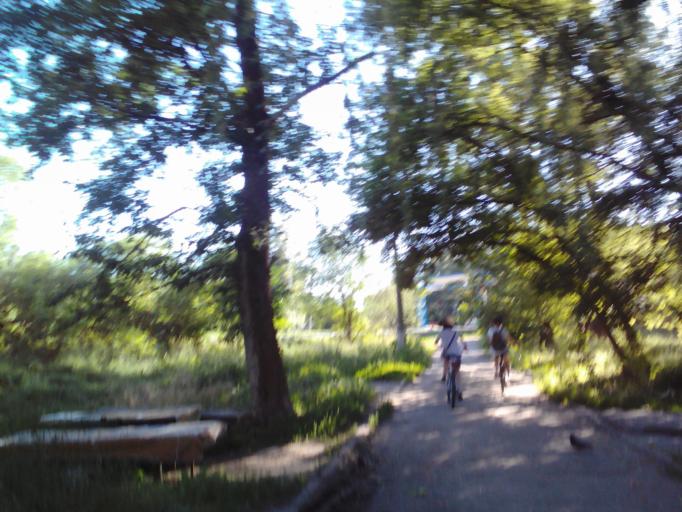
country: RU
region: Kursk
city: Voroshnevo
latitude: 51.6681
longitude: 36.0767
